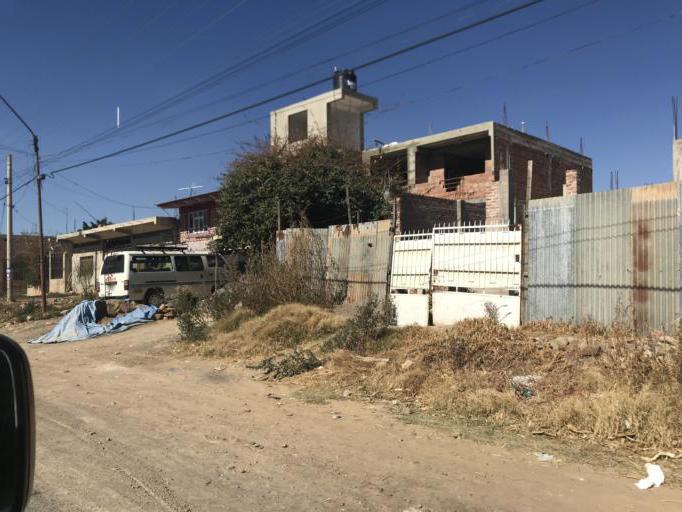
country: BO
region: Cochabamba
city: Cliza
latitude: -17.5771
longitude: -65.9066
